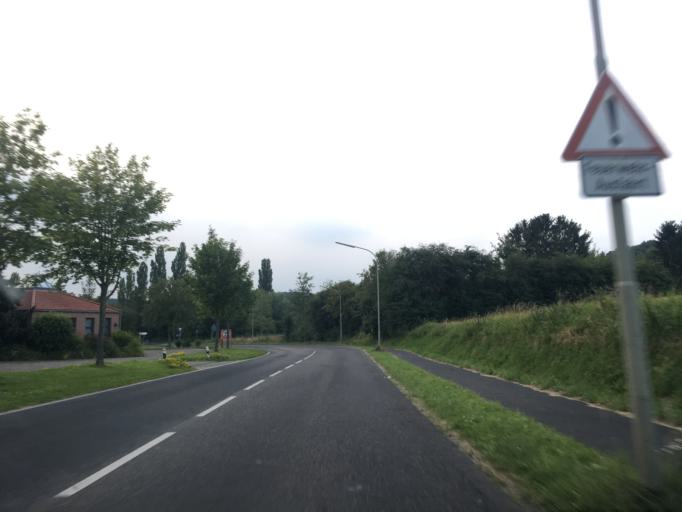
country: DE
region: North Rhine-Westphalia
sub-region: Regierungsbezirk Koln
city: Wassenberg
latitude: 51.0735
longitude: 6.1877
